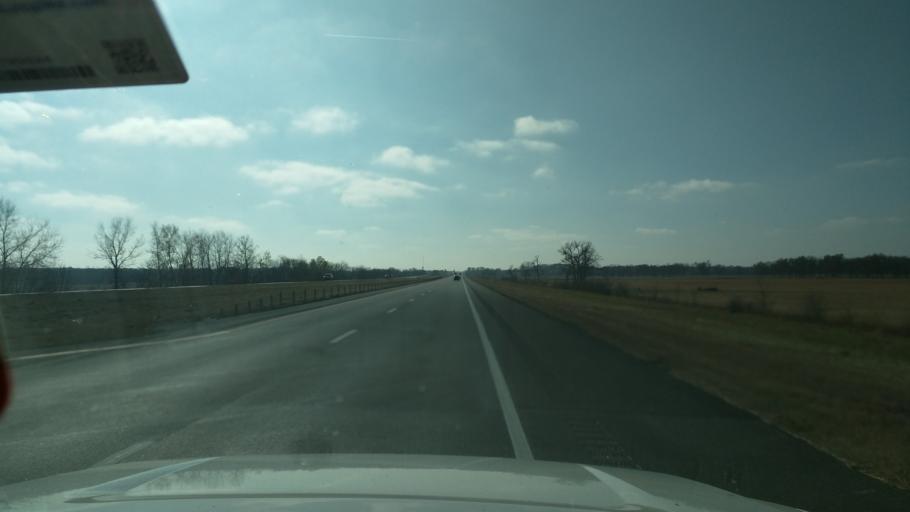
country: US
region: Oklahoma
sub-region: Washington County
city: Bartlesville
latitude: 36.6628
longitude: -95.9356
